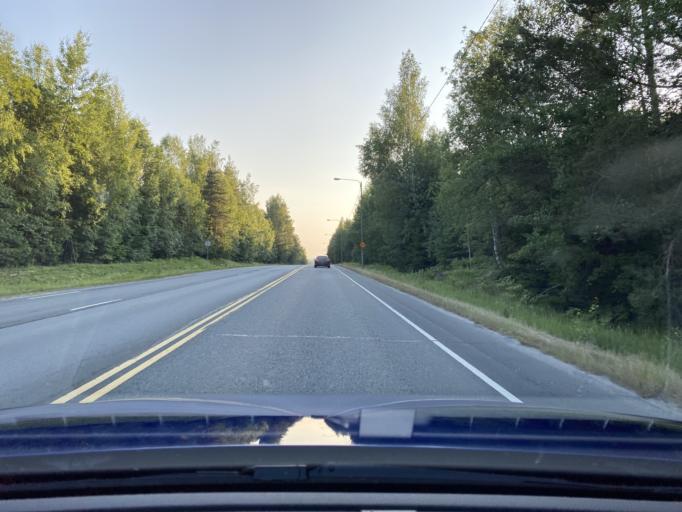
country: FI
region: Haeme
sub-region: Forssa
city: Forssa
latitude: 60.8285
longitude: 23.6488
